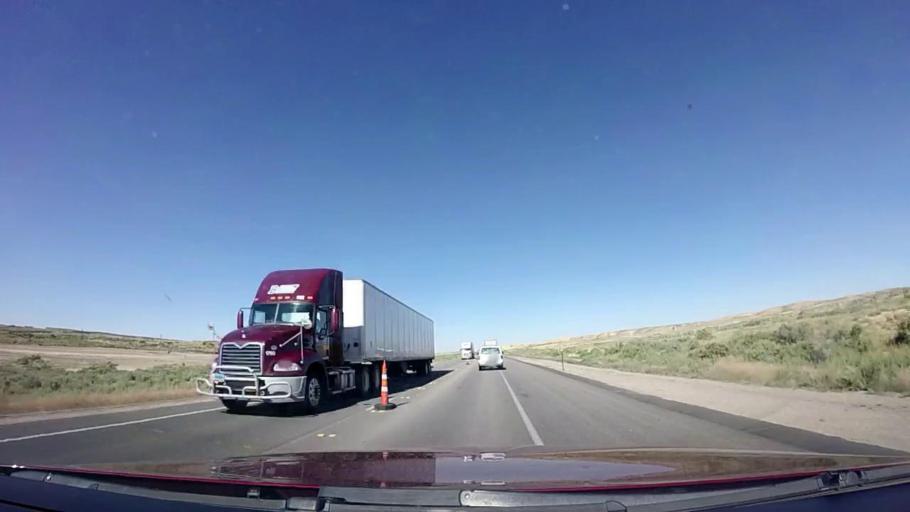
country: US
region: Wyoming
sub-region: Carbon County
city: Rawlins
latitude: 41.7064
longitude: -107.8606
